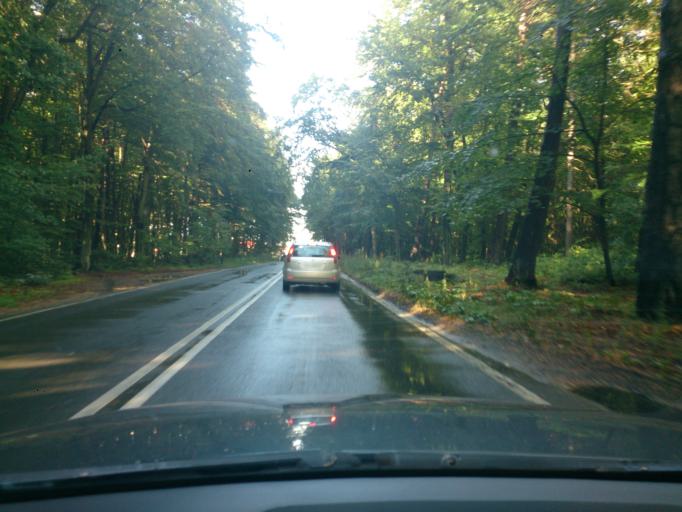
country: PL
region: Pomeranian Voivodeship
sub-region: Gdynia
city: Wielki Kack
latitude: 54.4635
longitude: 18.5087
